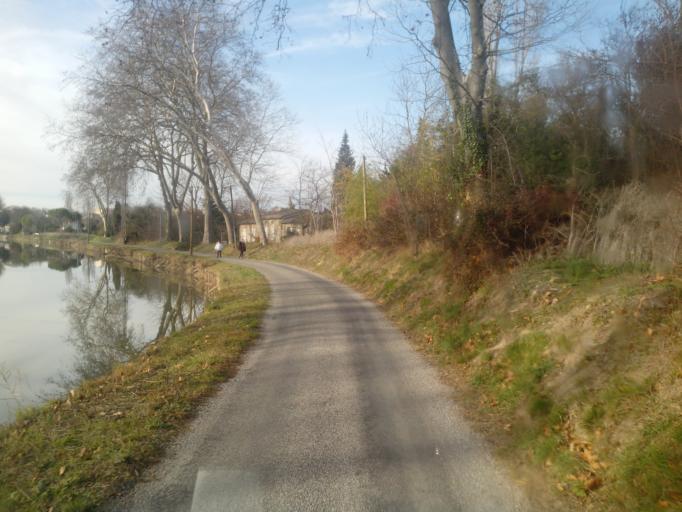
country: FR
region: Languedoc-Roussillon
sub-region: Departement de l'Aude
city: Castelnaudary
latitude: 43.3105
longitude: 1.9668
